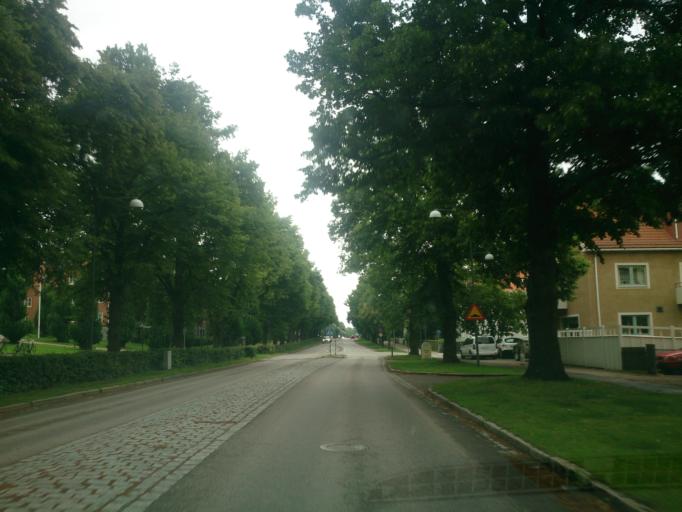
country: SE
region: OEstergoetland
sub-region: Linkopings Kommun
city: Linkoping
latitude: 58.4041
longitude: 15.6116
